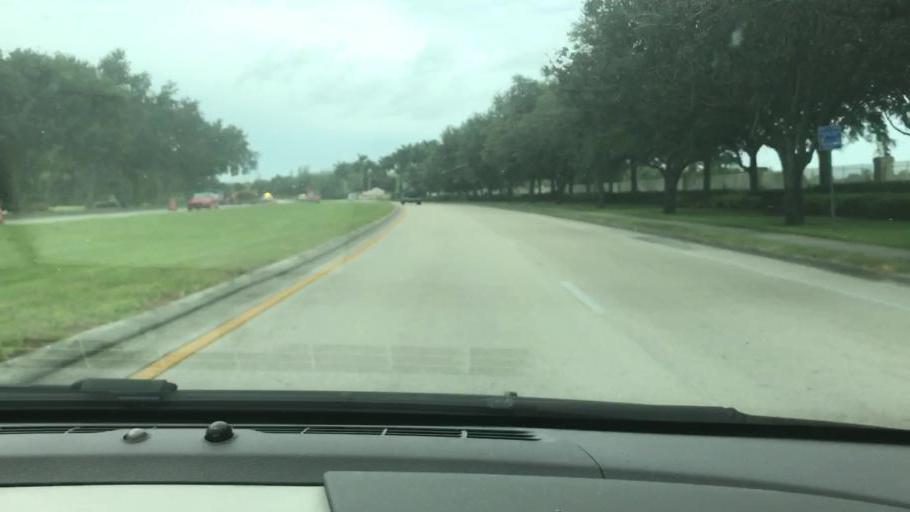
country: US
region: Florida
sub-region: Lee County
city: Palmona Park
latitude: 26.7109
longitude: -81.9405
